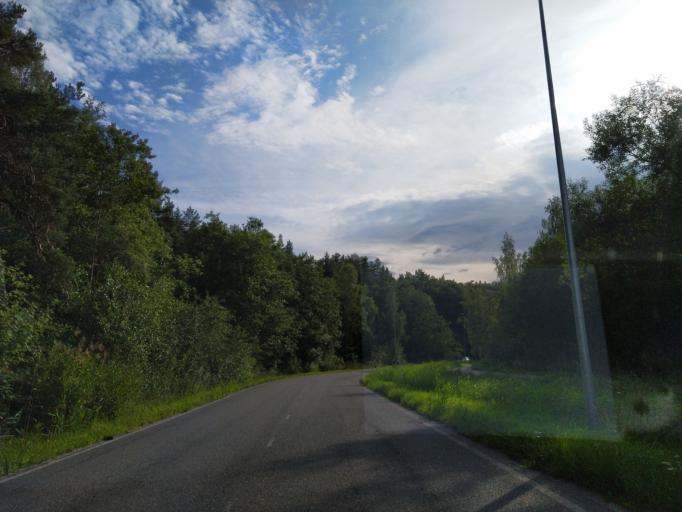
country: FI
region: Varsinais-Suomi
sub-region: Turku
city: Turku
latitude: 60.4284
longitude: 22.2147
